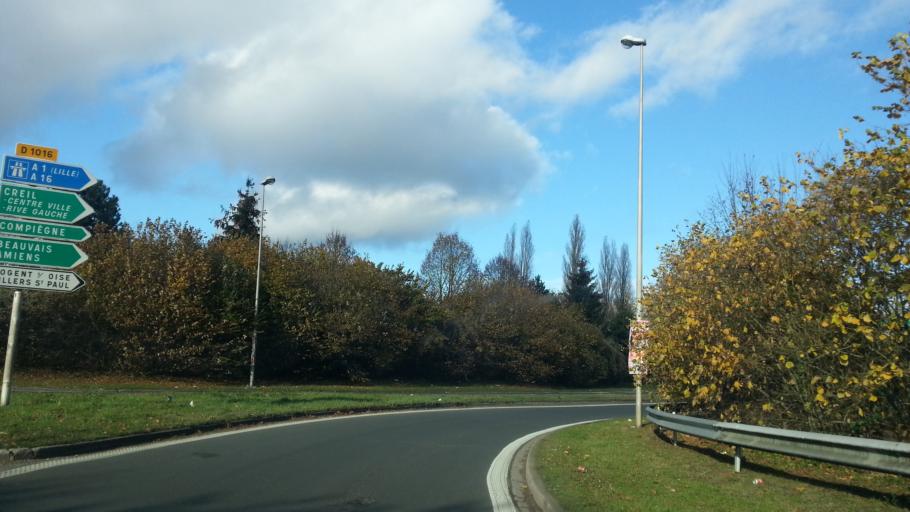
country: FR
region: Picardie
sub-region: Departement de l'Oise
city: Creil
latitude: 49.2456
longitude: 2.4753
